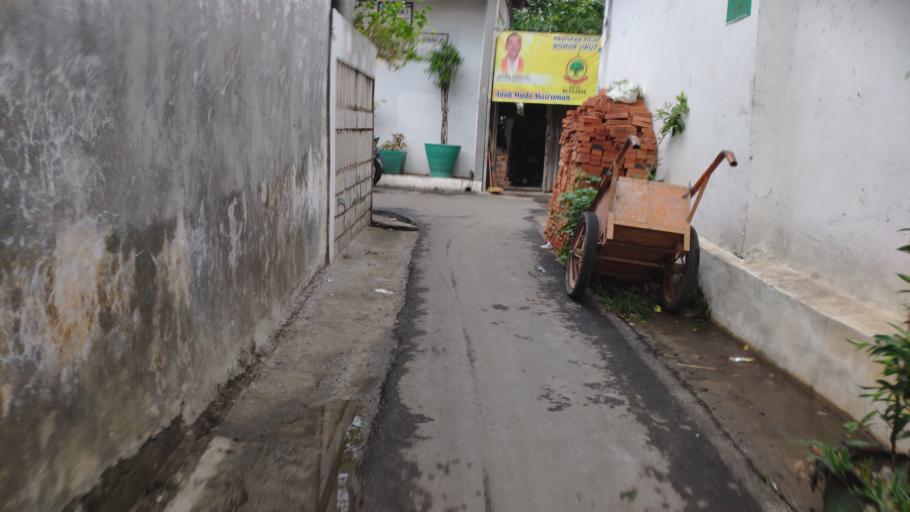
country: ID
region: Jakarta Raya
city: Jakarta
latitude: -6.2011
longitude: 106.8589
